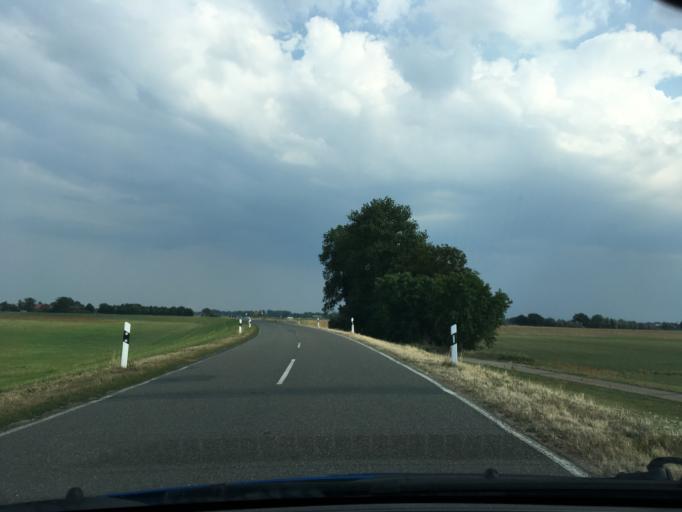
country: DE
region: Lower Saxony
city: Hitzacker
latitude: 53.1413
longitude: 11.0669
